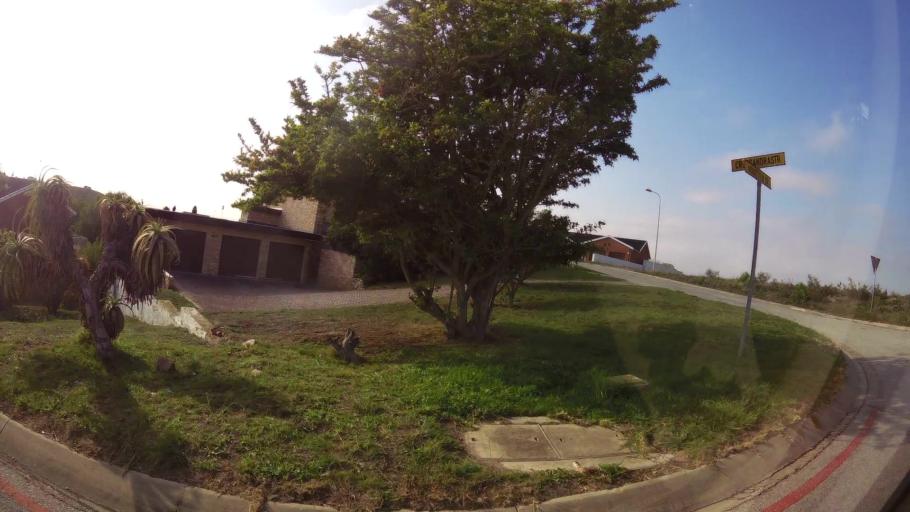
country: ZA
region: Eastern Cape
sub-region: Nelson Mandela Bay Metropolitan Municipality
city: Port Elizabeth
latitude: -33.9310
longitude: 25.5485
